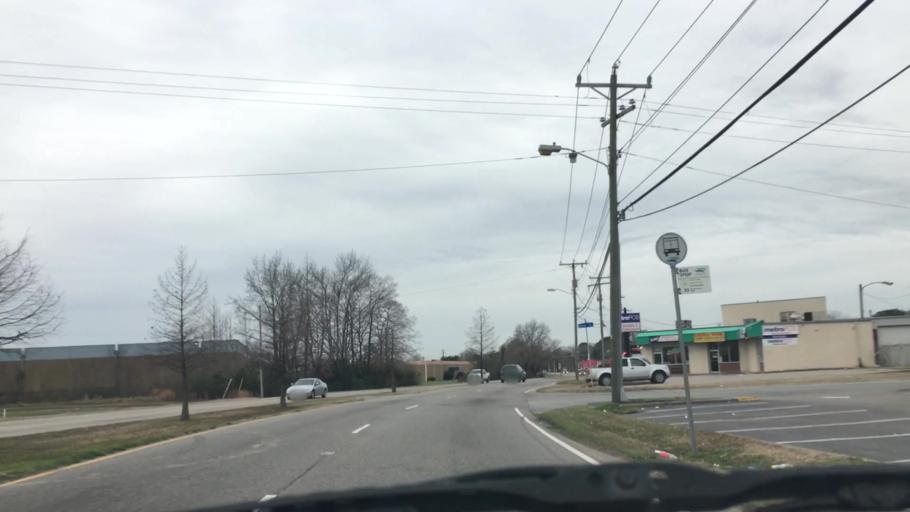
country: US
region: Virginia
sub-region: City of Norfolk
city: Norfolk
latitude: 36.8672
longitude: -76.2314
